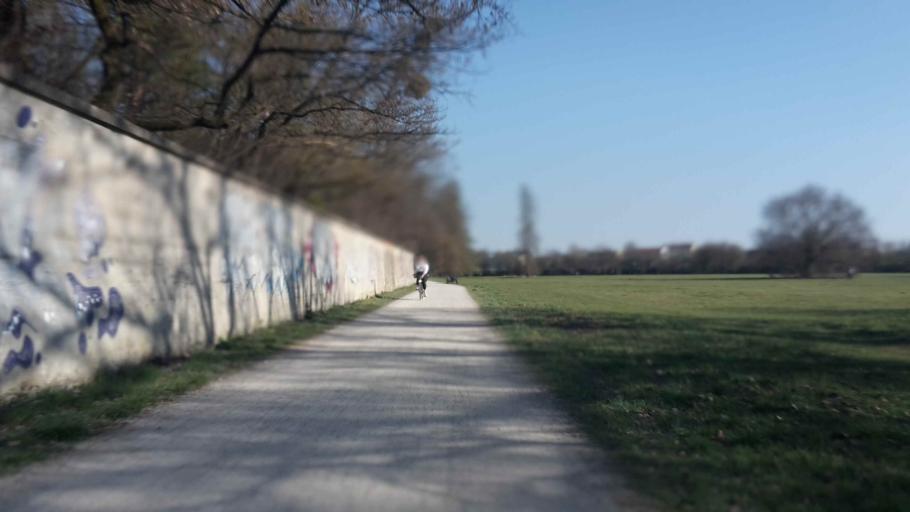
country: DE
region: Bavaria
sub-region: Upper Bavaria
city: Pasing
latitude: 48.1513
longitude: 11.4914
